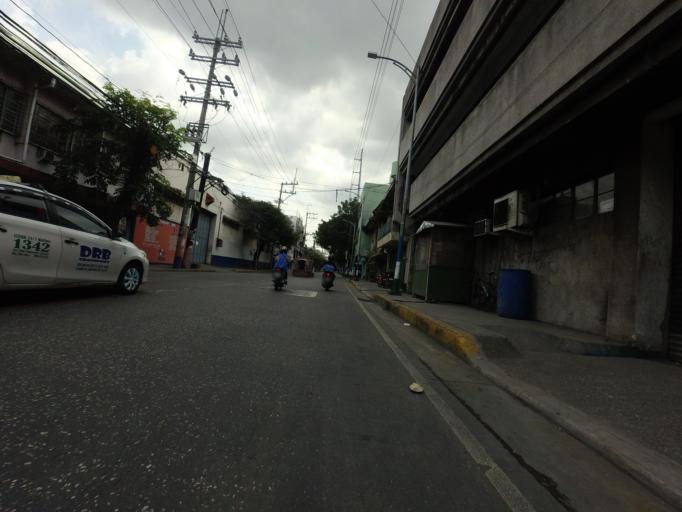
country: PH
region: Metro Manila
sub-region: City of Manila
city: Quiapo
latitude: 14.5813
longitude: 120.9972
